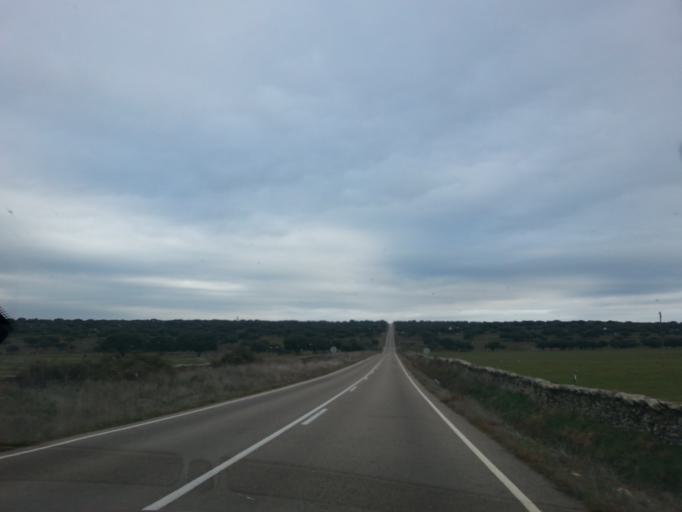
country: ES
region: Castille and Leon
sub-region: Provincia de Salamanca
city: Vecinos
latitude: 40.7554
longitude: -5.9061
